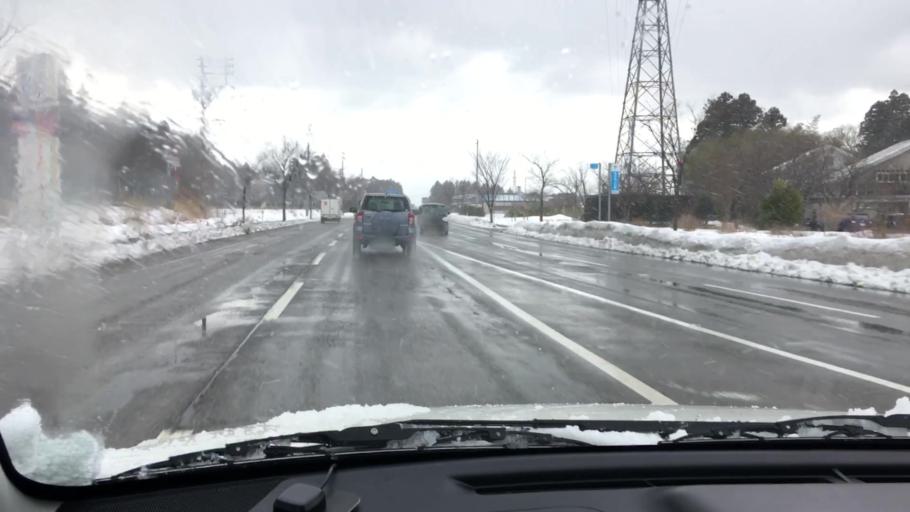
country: JP
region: Niigata
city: Joetsu
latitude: 37.0989
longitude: 138.2309
